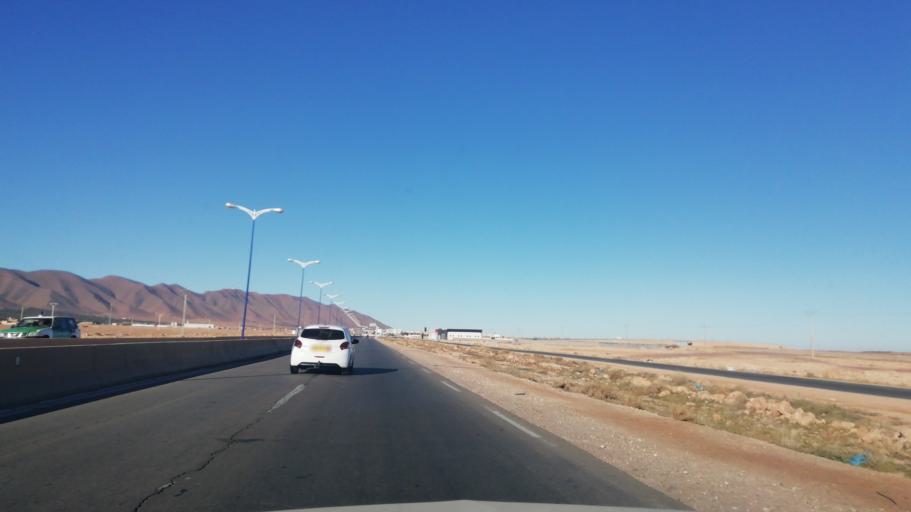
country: DZ
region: Wilaya de Naama
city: Naama
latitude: 33.5037
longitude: -0.2877
